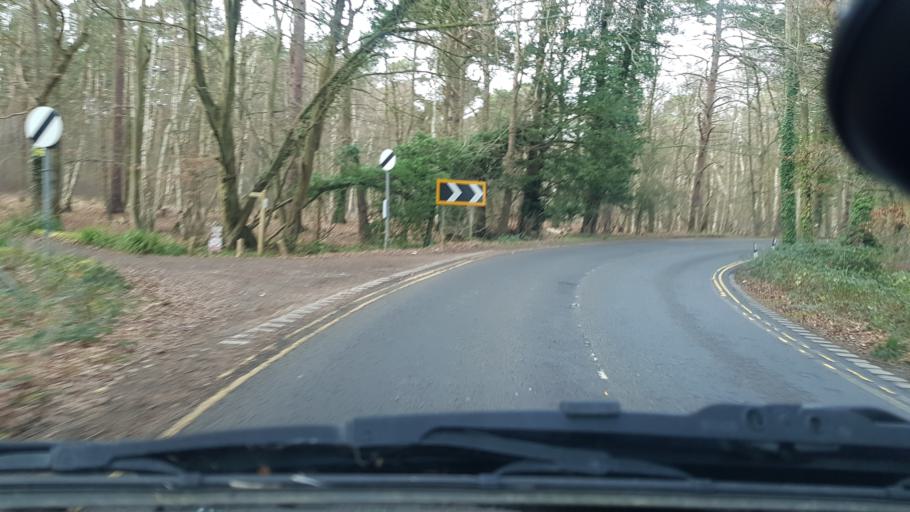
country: GB
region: England
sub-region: Surrey
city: Byfleet
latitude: 51.3122
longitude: -0.4518
